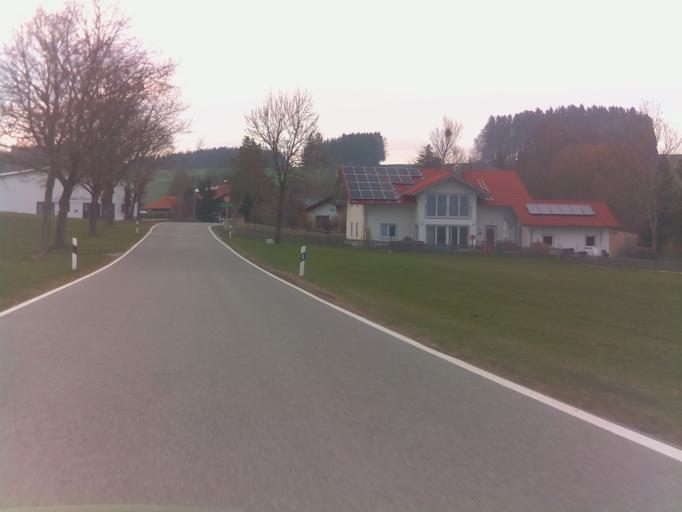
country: DE
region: Bavaria
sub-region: Upper Bavaria
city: Ingenried
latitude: 47.8245
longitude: 10.7811
